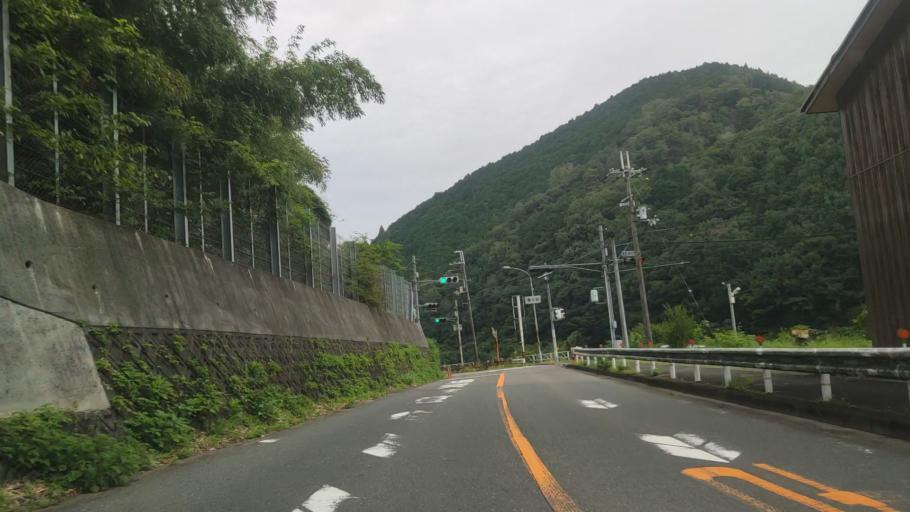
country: JP
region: Wakayama
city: Hashimoto
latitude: 34.3913
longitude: 135.5982
